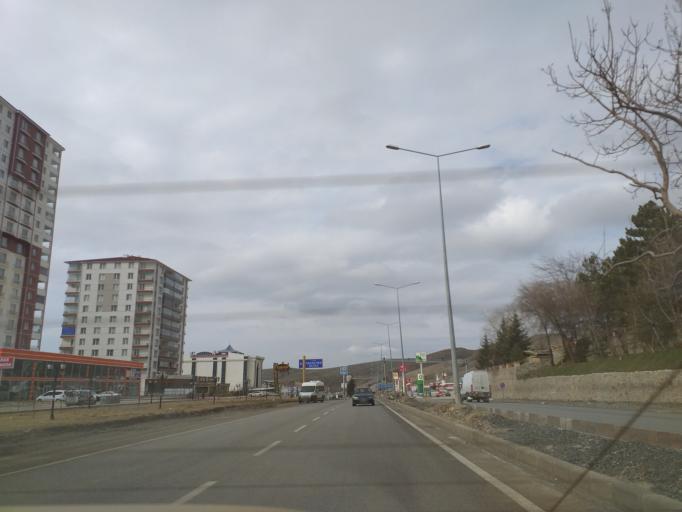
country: TR
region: Yozgat
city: Yozgat
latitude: 39.8178
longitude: 34.7926
